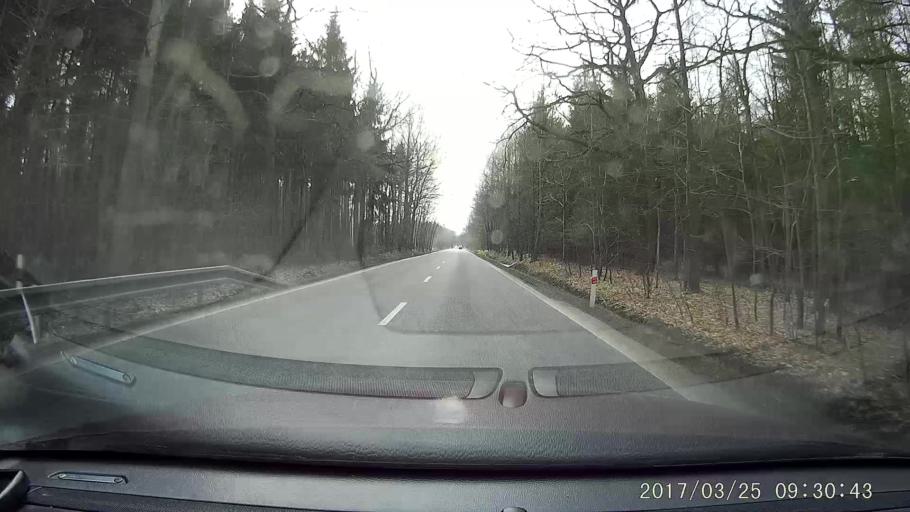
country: PL
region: Silesian Voivodeship
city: Zawidow
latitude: 50.9996
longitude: 15.0732
